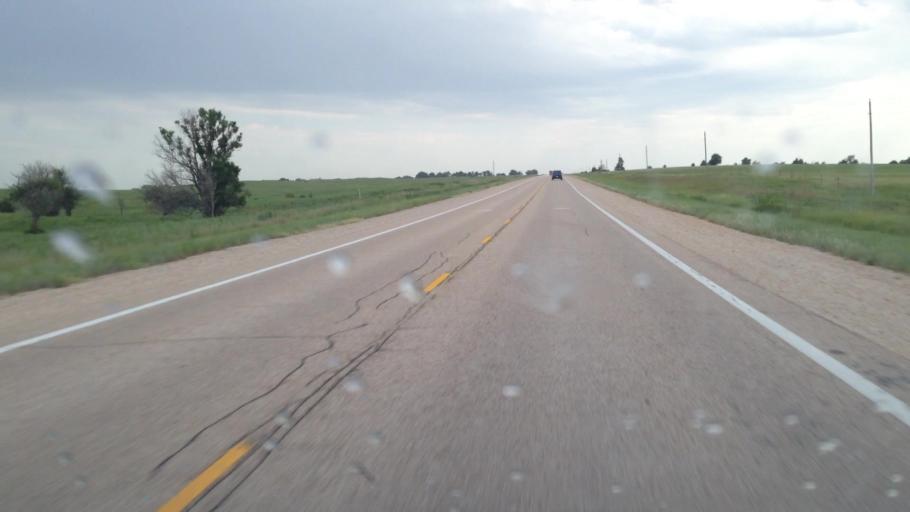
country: US
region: Kansas
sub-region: Coffey County
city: Burlington
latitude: 38.1532
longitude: -95.7388
